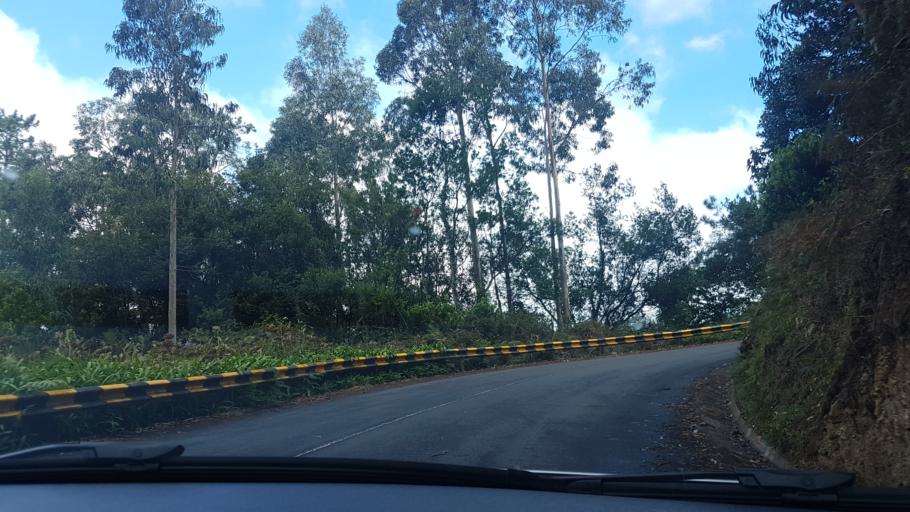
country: PT
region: Madeira
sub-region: Sao Vicente
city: Sao Vicente
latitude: 32.7653
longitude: -17.0284
